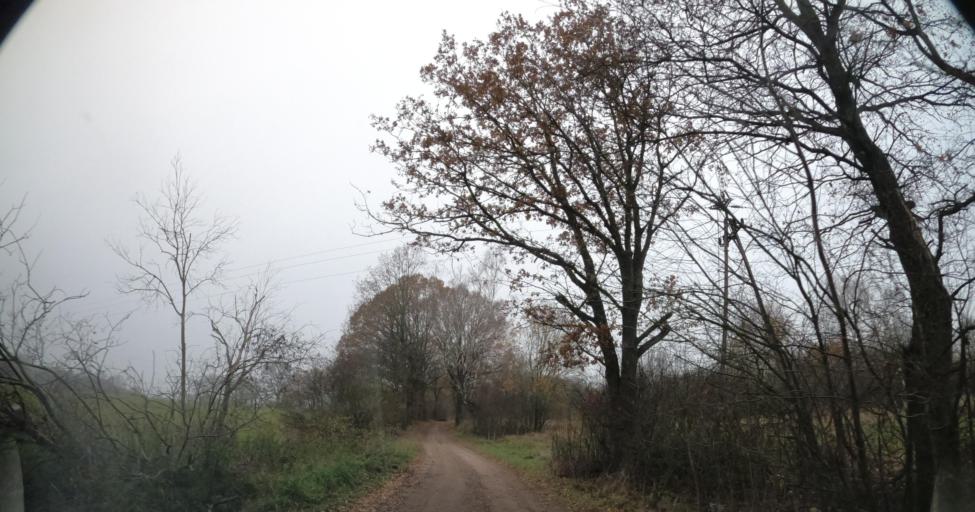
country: PL
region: West Pomeranian Voivodeship
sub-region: Powiat drawski
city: Drawsko Pomorskie
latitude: 53.5880
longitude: 15.7990
